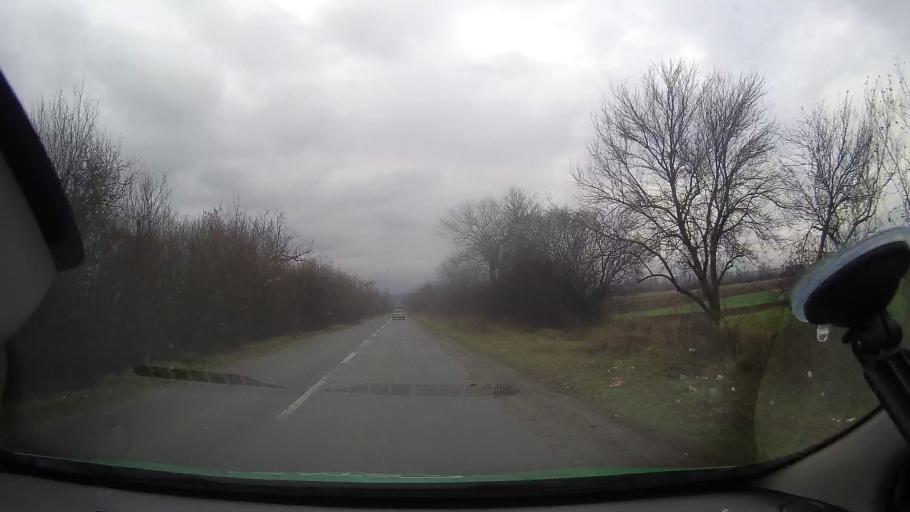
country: RO
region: Arad
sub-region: Comuna Sebis
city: Sebis
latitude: 46.3571
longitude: 22.1305
